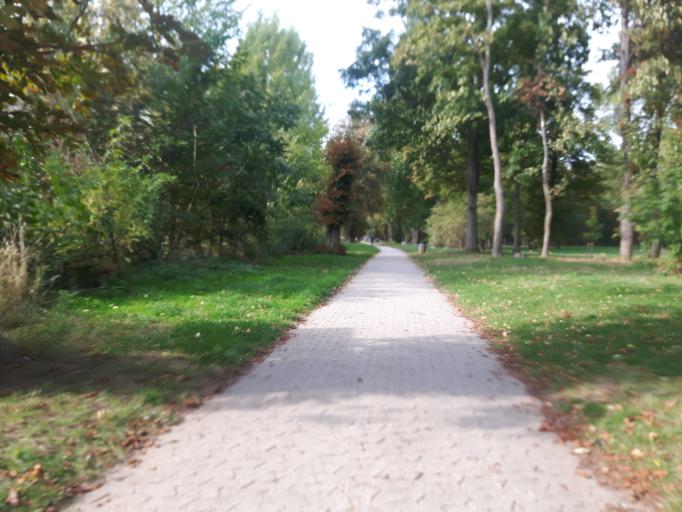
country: DE
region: Rheinland-Pfalz
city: Weissenthurm
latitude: 50.4363
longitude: 7.4488
